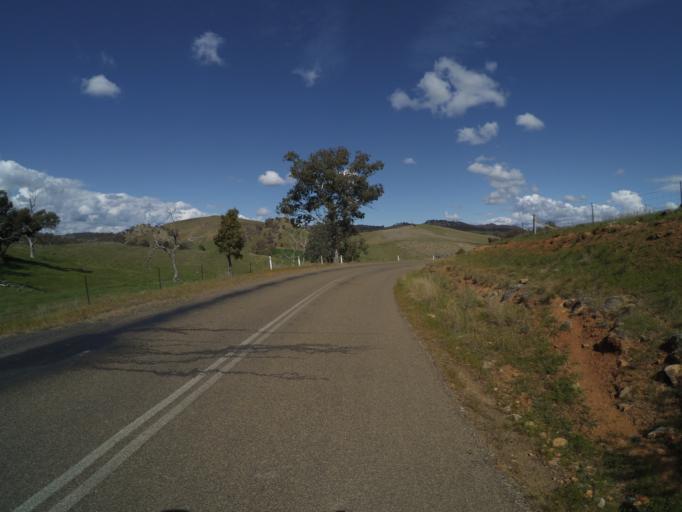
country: AU
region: New South Wales
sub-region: Yass Valley
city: Murrumbateman
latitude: -35.0125
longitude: 148.8536
